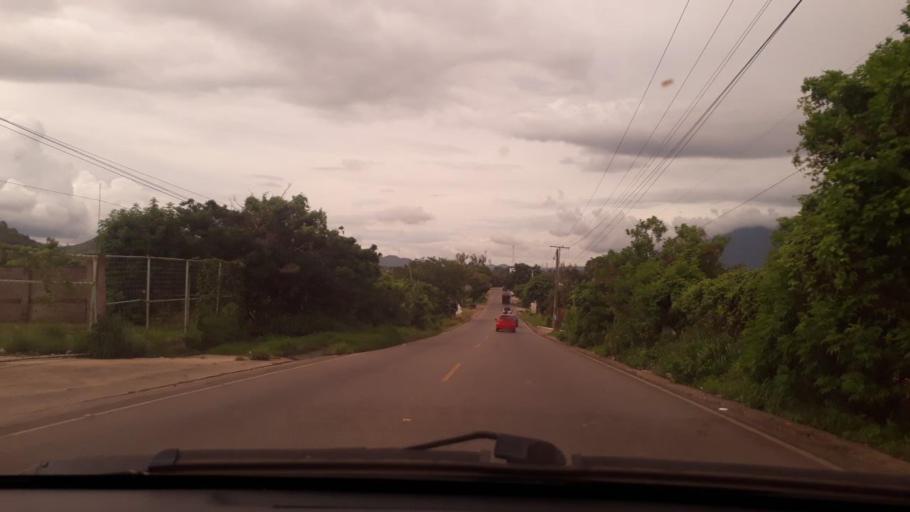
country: GT
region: Jutiapa
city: Jutiapa
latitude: 14.3086
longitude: -89.8691
